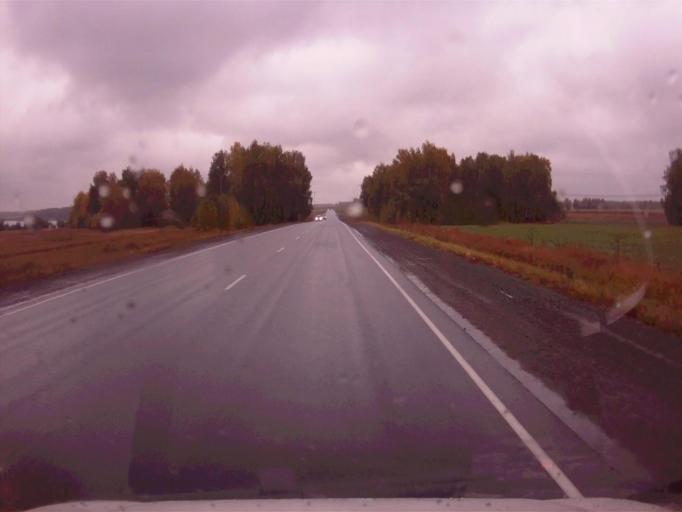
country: RU
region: Chelyabinsk
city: Roshchino
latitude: 55.3866
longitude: 61.1306
